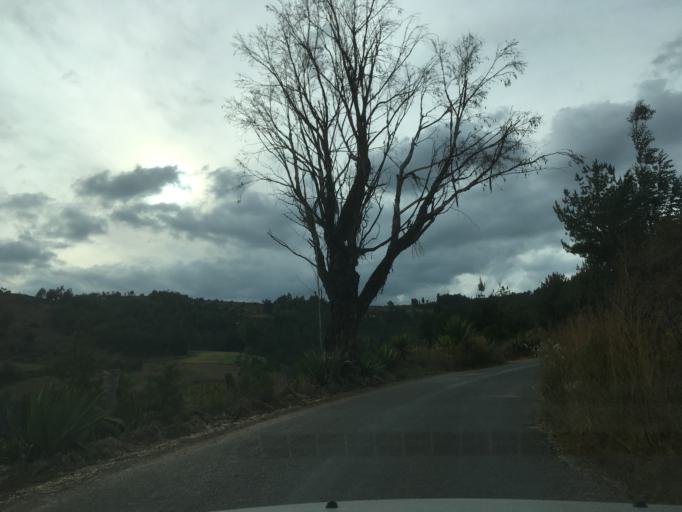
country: CO
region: Boyaca
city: Firavitoba
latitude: 5.6788
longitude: -73.0104
